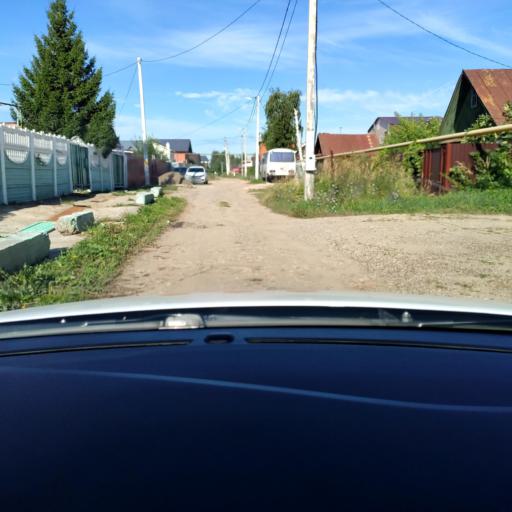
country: RU
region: Tatarstan
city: Verkhniy Uslon
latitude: 55.8019
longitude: 49.0344
